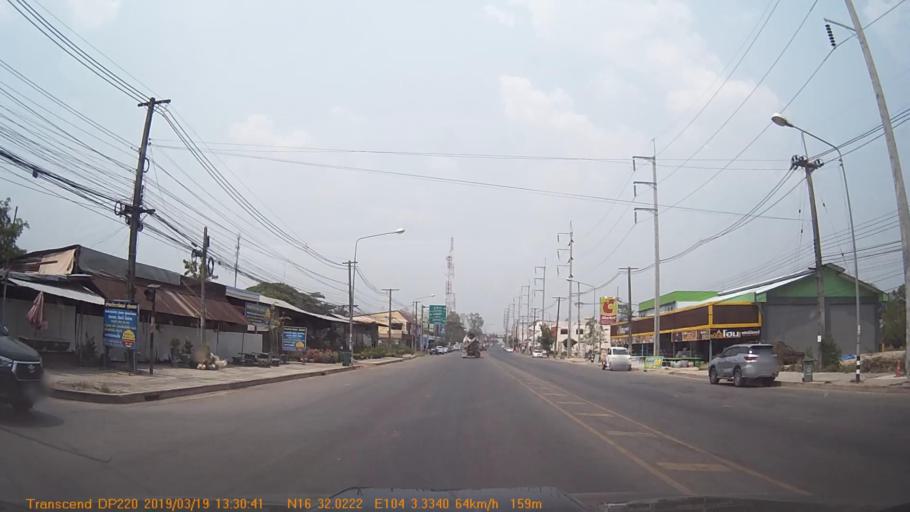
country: TH
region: Kalasin
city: Kuchinarai
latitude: 16.5340
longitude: 104.0555
